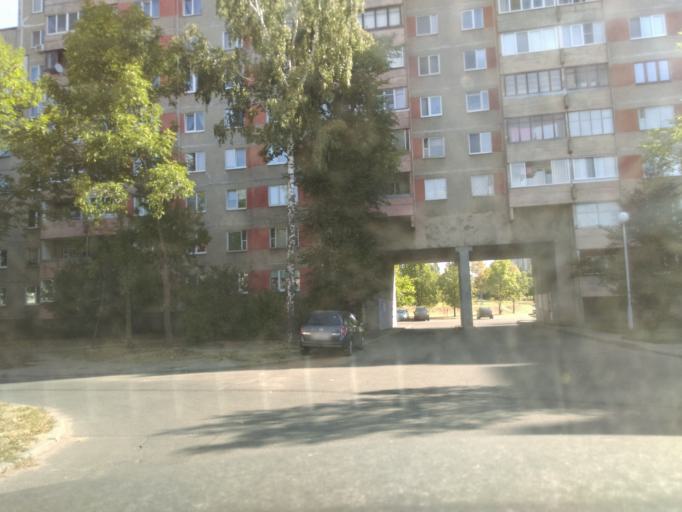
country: BY
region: Minsk
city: Minsk
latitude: 53.8512
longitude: 27.5986
